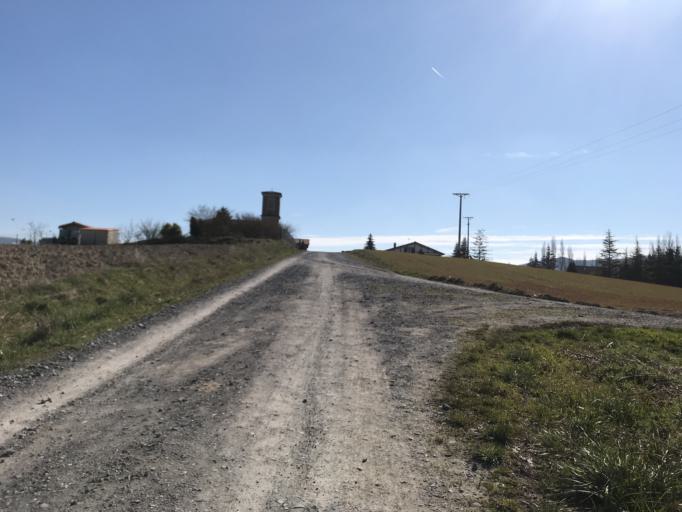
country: ES
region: Basque Country
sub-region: Provincia de Alava
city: Gasteiz / Vitoria
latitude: 42.8213
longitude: -2.6532
